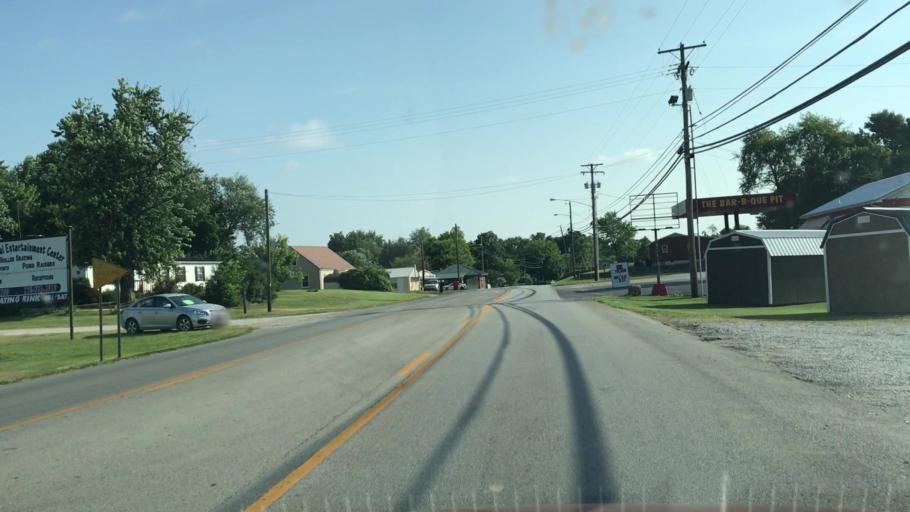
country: US
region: Kentucky
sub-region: Barren County
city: Cave City
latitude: 37.1317
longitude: -85.9598
